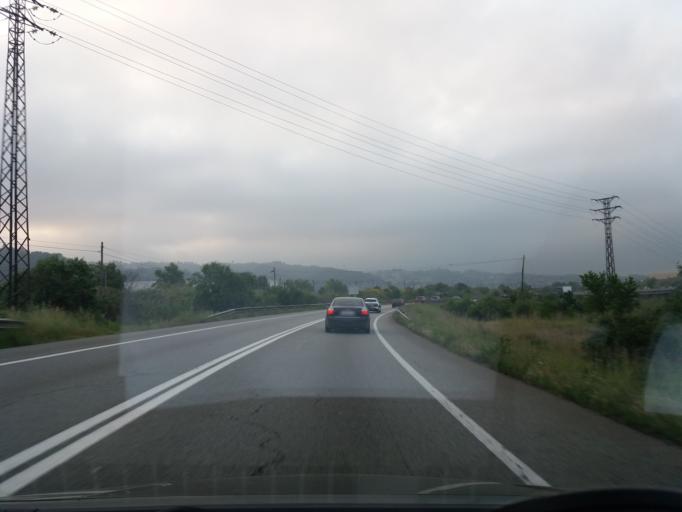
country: ES
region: Catalonia
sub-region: Provincia de Barcelona
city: Olesa de Montserrat
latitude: 41.5368
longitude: 1.8966
